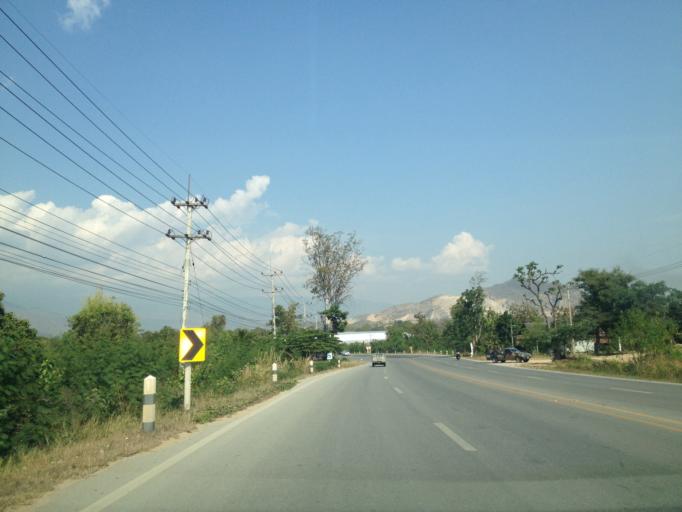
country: TH
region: Chiang Mai
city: Hot
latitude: 18.2167
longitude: 98.6151
